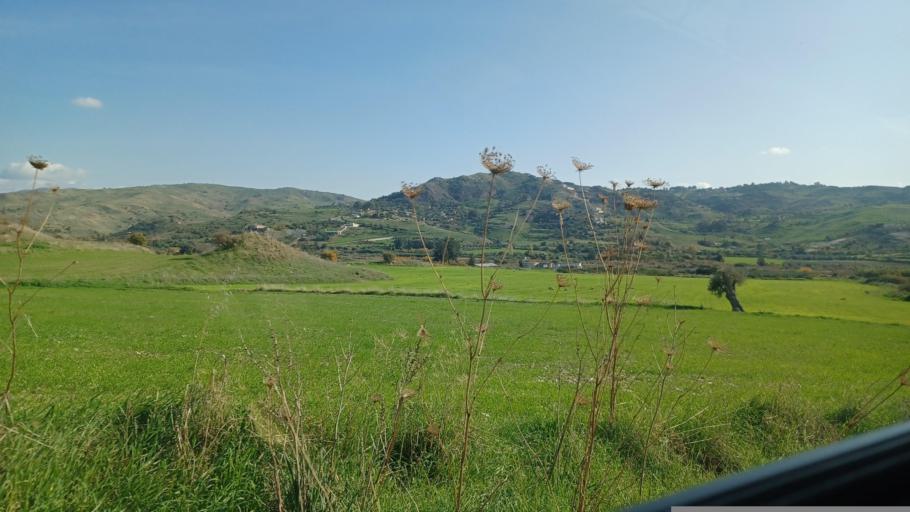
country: CY
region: Pafos
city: Mesogi
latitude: 34.7731
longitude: 32.5738
